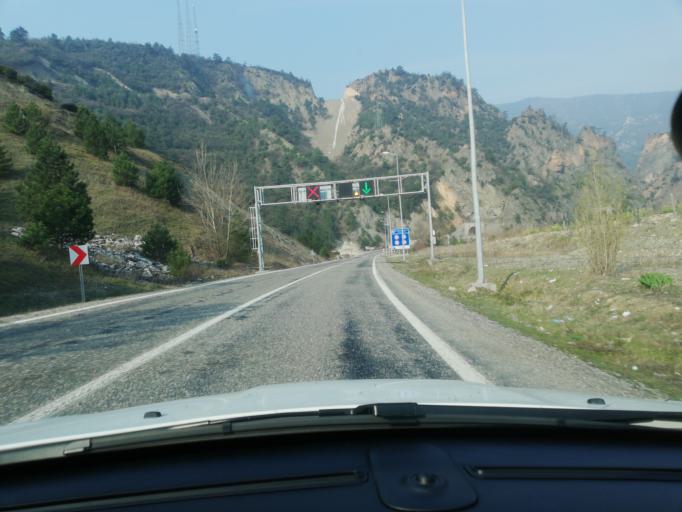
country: TR
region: Karabuk
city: Karabuk
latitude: 41.1520
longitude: 32.5334
